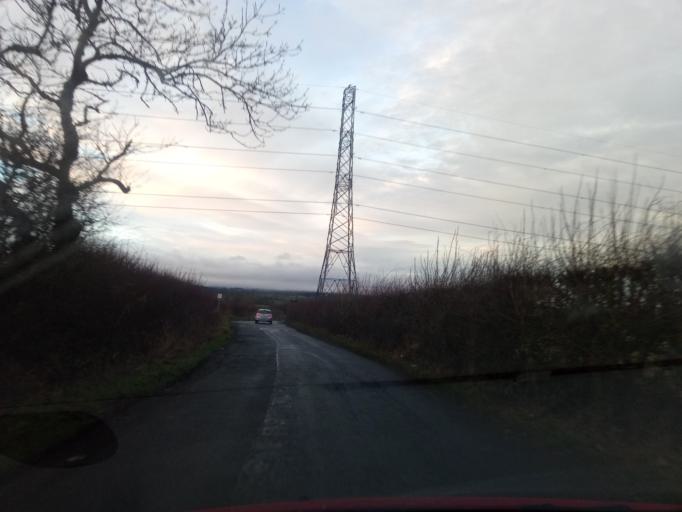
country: GB
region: England
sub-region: Northumberland
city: Ponteland
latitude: 55.0784
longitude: -1.7368
